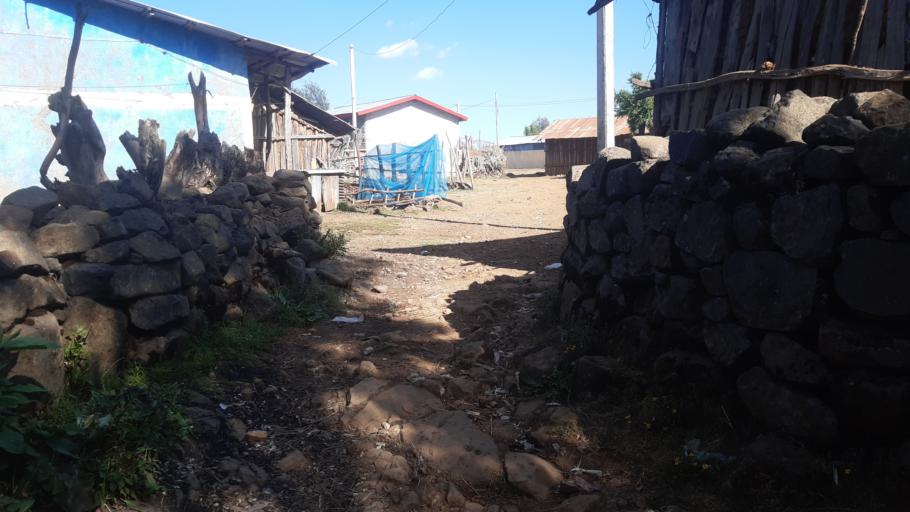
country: ET
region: Amhara
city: Dabat
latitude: 13.3504
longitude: 37.3896
